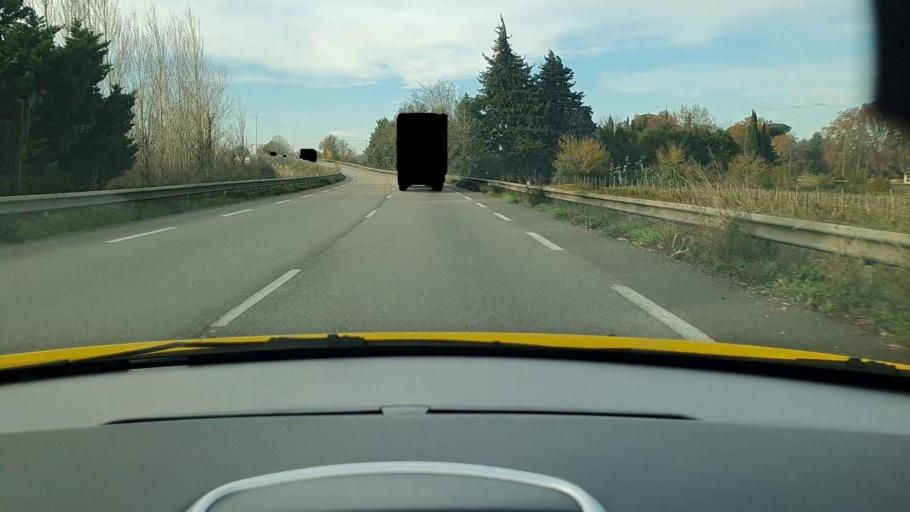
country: FR
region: Languedoc-Roussillon
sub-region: Departement du Gard
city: Beaucaire
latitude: 43.7937
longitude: 4.6249
